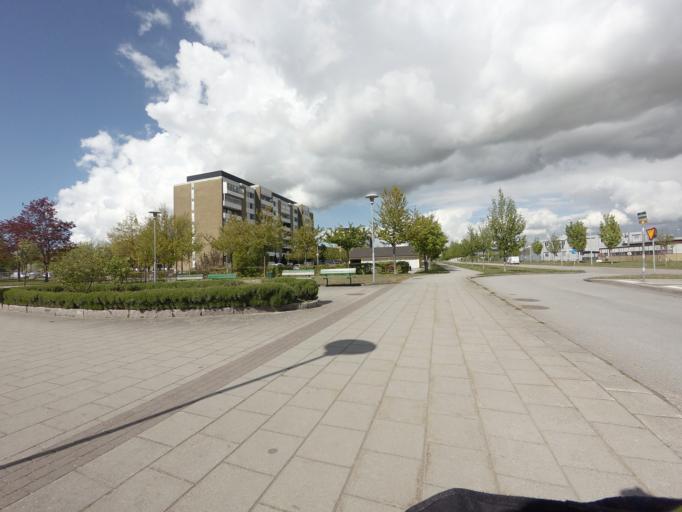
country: SE
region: Skane
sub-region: Landskrona
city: Landskrona
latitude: 55.8900
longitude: 12.8505
